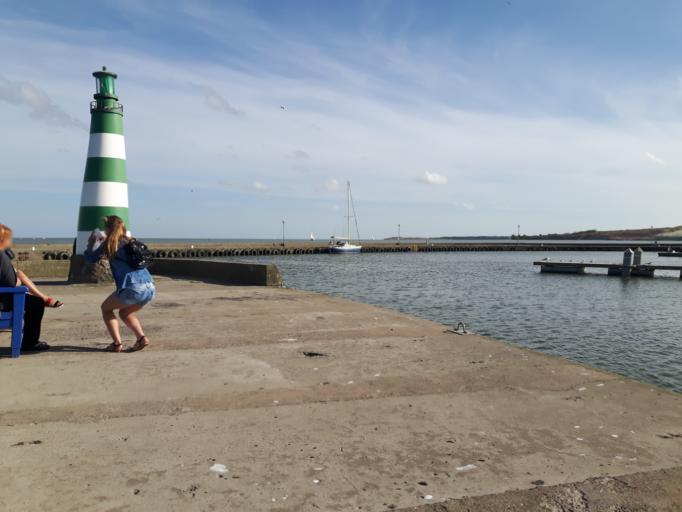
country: LT
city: Nida
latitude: 55.3019
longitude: 21.0103
